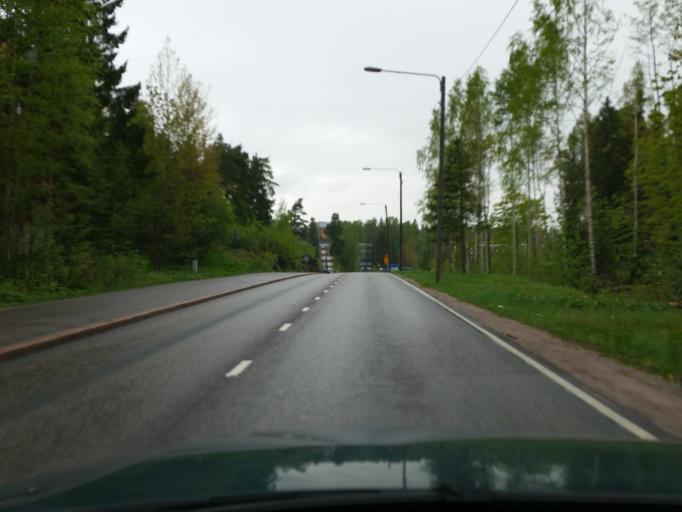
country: FI
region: Uusimaa
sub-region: Helsinki
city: Teekkarikylae
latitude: 60.2227
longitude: 24.8295
